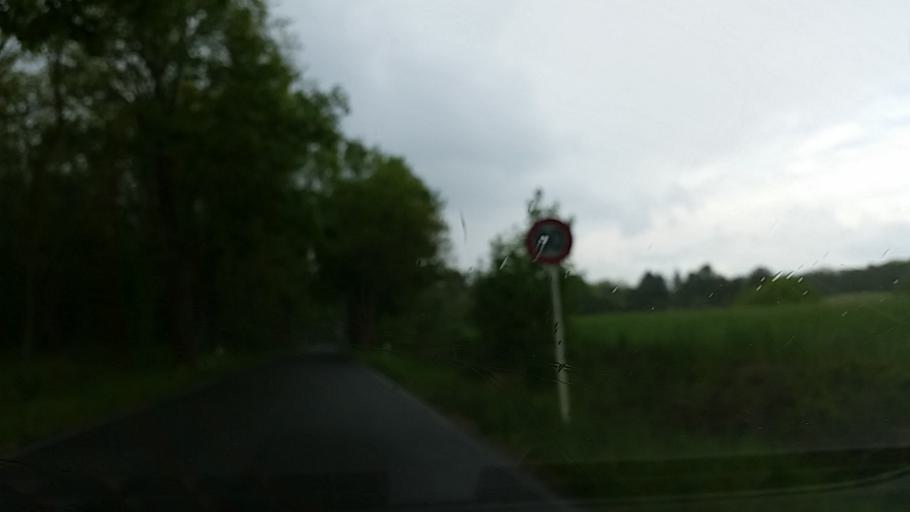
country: DE
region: Brandenburg
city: Diensdorf-Radlow
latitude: 52.2559
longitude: 14.0397
